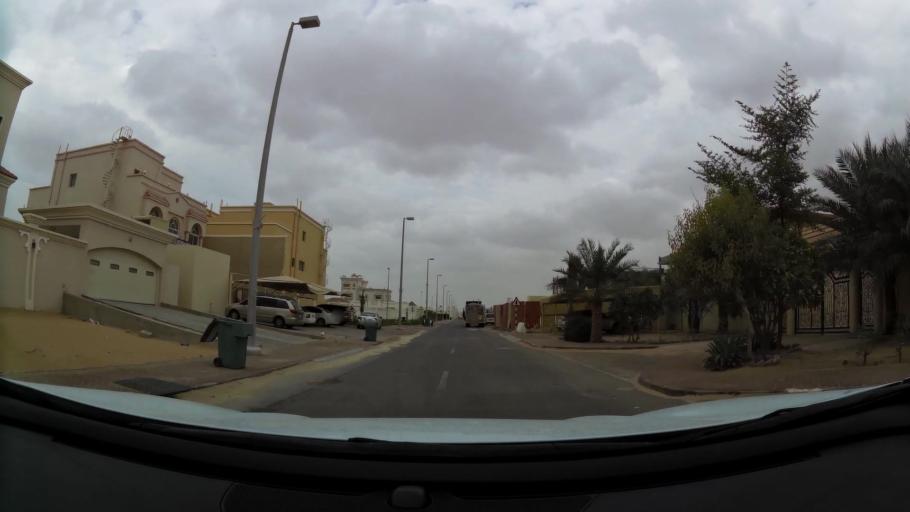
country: AE
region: Abu Dhabi
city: Abu Dhabi
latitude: 24.3749
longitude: 54.6338
